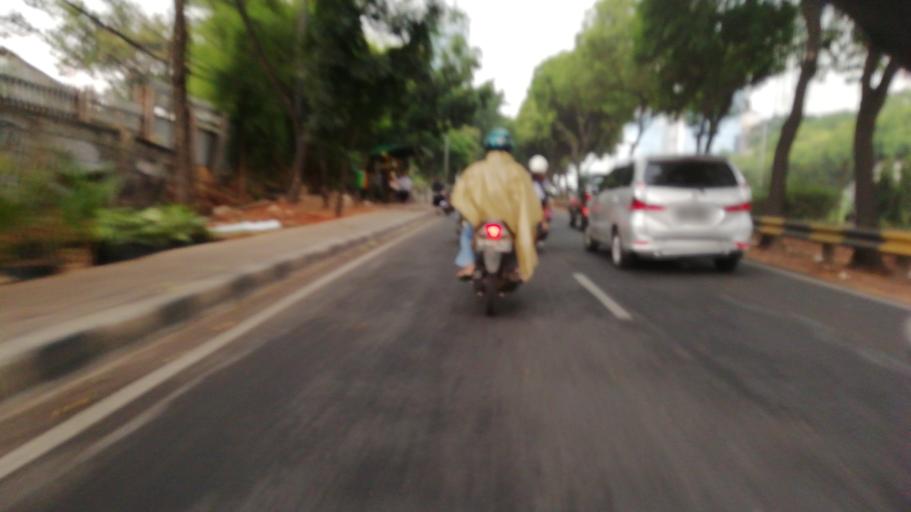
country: ID
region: Jakarta Raya
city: Jakarta
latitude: -6.2976
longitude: 106.8306
